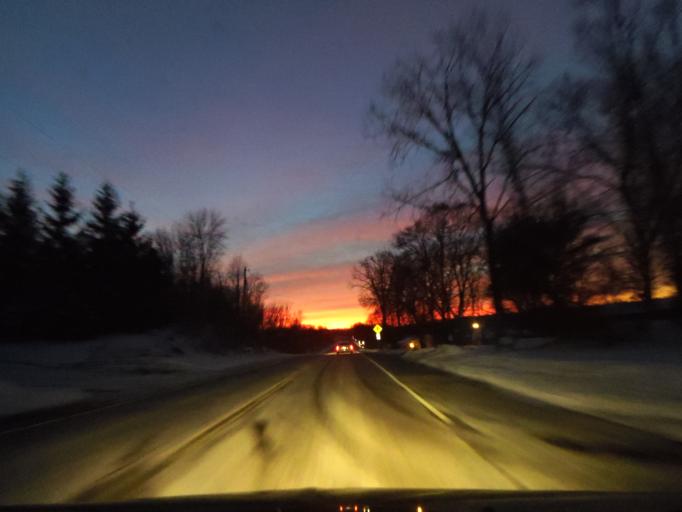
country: US
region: Minnesota
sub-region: Chisago County
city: Chisago City
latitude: 45.3433
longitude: -92.8613
